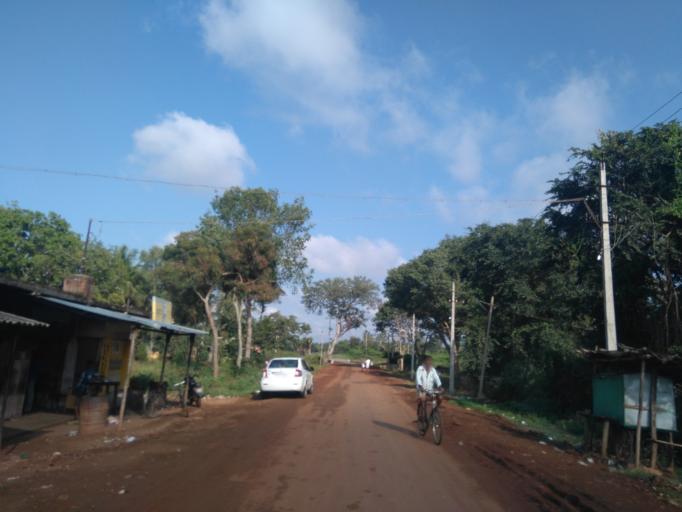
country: IN
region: Karnataka
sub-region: Mysore
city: Tirumakudal Narsipur
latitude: 12.2582
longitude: 77.0079
